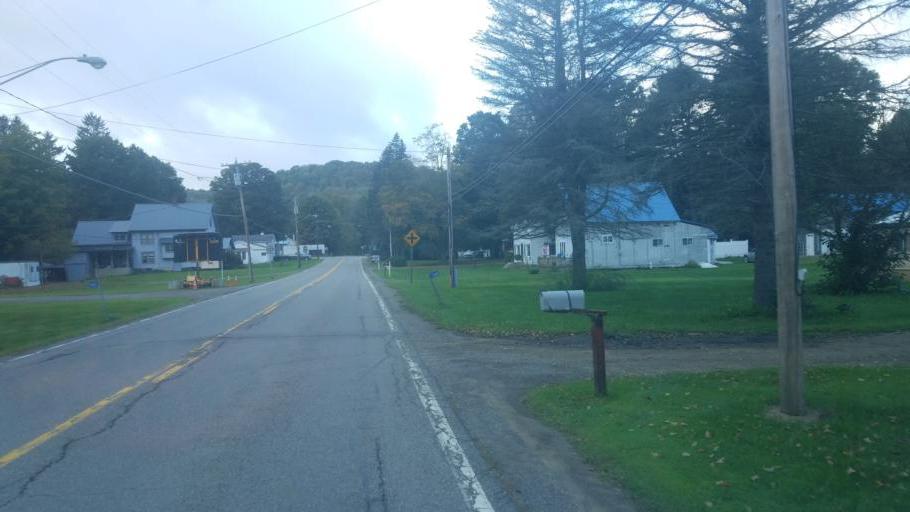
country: US
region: New York
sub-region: Cattaraugus County
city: Weston Mills
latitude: 42.1798
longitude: -78.3792
